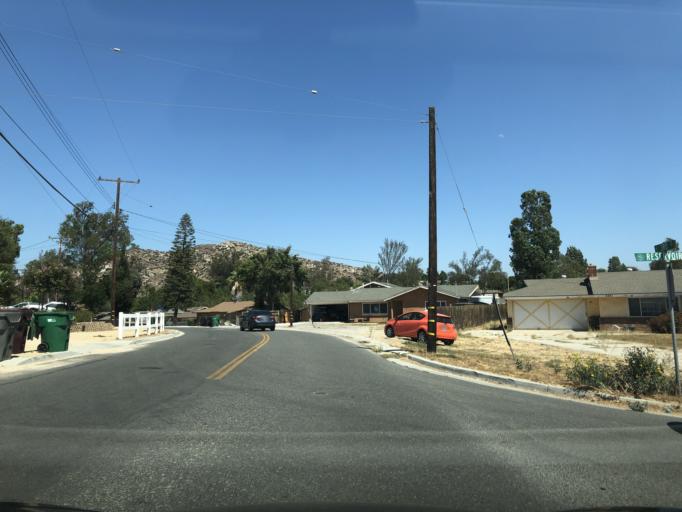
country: US
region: California
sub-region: Riverside County
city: Norco
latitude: 33.9174
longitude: -117.5521
